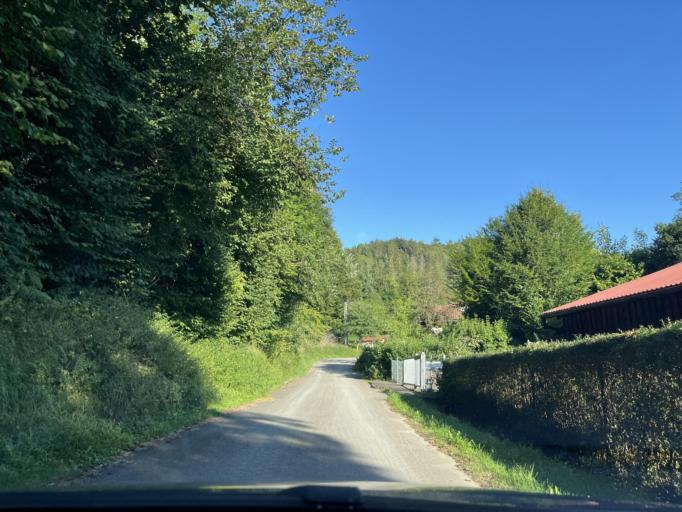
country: DE
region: Baden-Wuerttemberg
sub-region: Tuebingen Region
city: Veringenstadt
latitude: 48.1972
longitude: 9.2163
